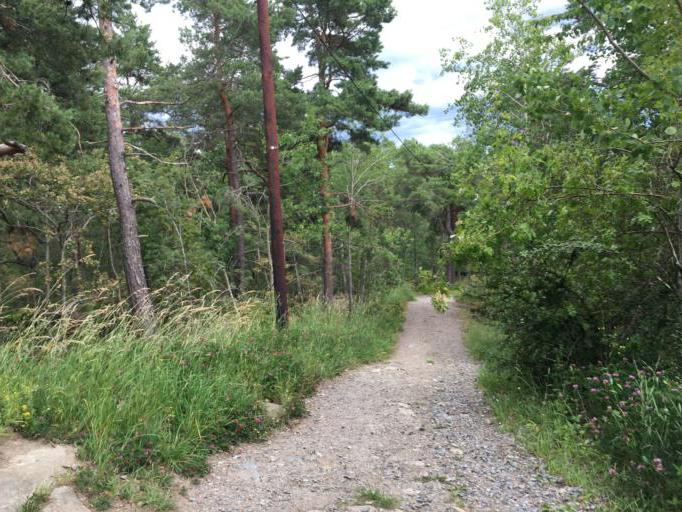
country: SE
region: Stockholm
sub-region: Nacka Kommun
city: Fisksatra
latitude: 59.3082
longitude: 18.2482
